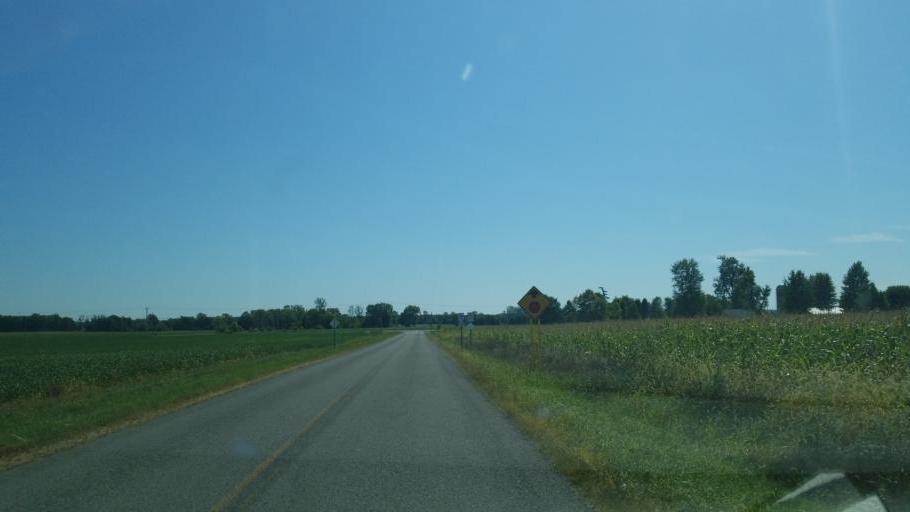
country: US
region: Ohio
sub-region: Logan County
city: Northwood
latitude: 40.5139
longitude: -83.7631
